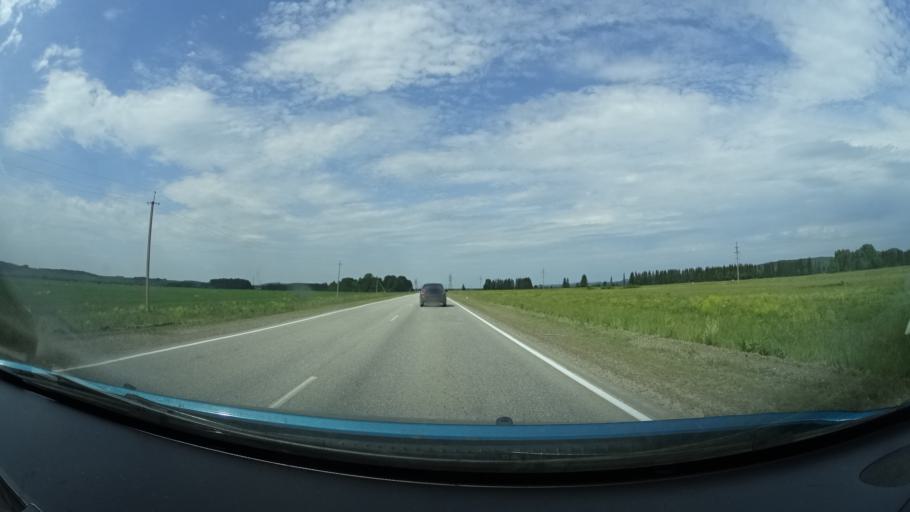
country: RU
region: Perm
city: Barda
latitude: 57.0632
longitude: 55.5421
